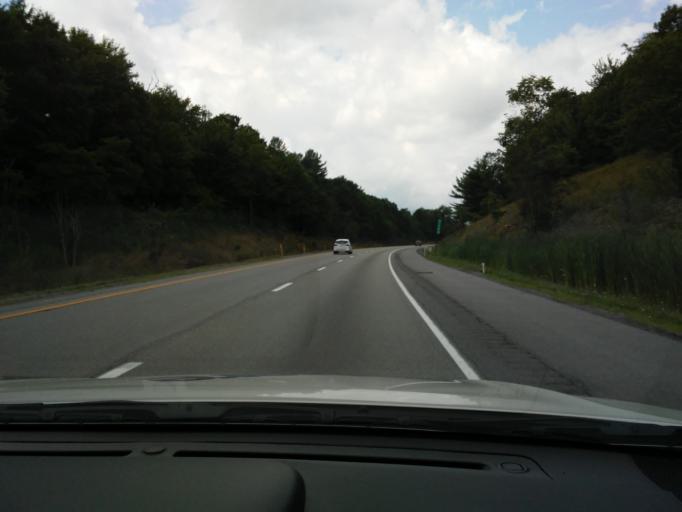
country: US
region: Pennsylvania
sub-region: Clearfield County
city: Troy
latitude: 40.9632
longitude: -78.1073
